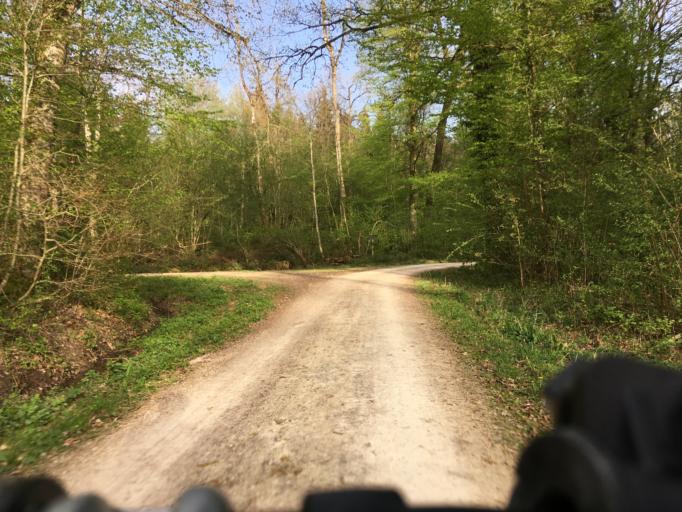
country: CH
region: Schaffhausen
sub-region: Bezirk Stein
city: Ramsen
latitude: 47.6833
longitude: 8.7911
